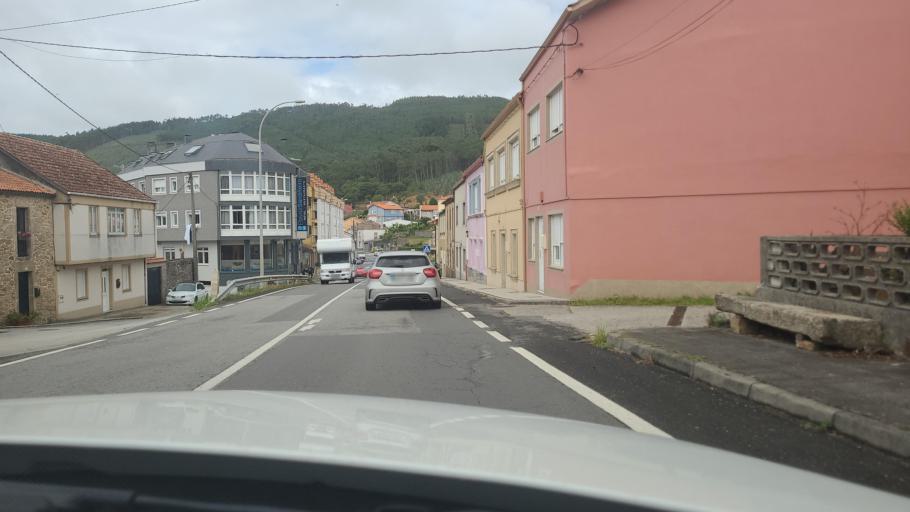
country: ES
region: Galicia
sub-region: Provincia da Coruna
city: Corcubion
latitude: 42.9434
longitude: -9.2303
